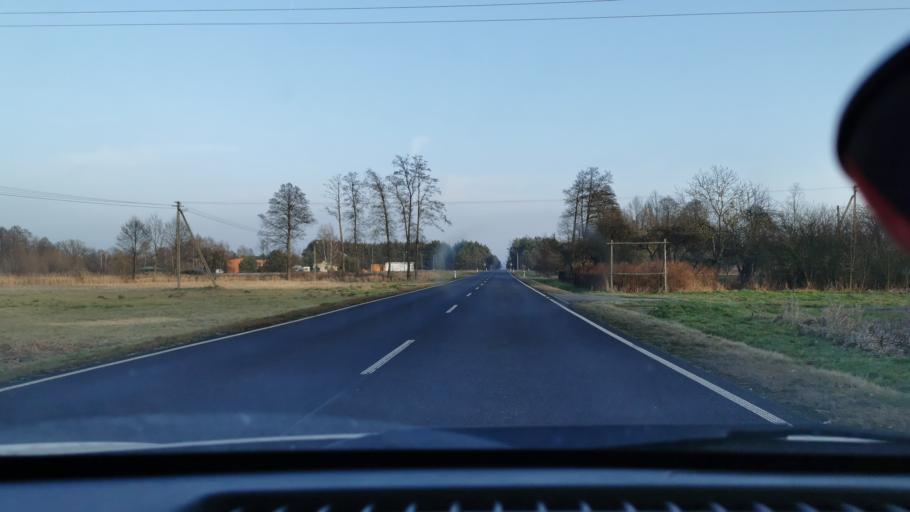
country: PL
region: Lodz Voivodeship
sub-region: Powiat pabianicki
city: Dlutow
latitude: 51.5121
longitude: 19.3421
